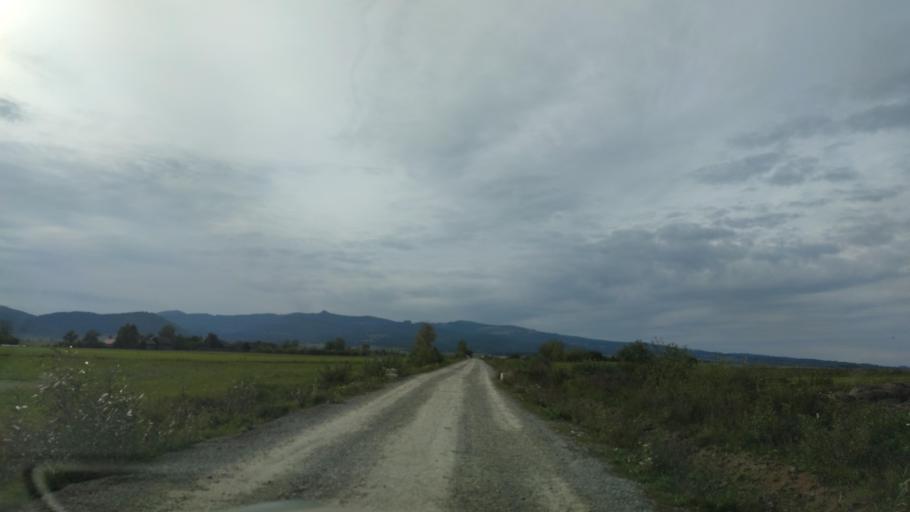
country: RO
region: Harghita
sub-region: Comuna Remetea
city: Remetea
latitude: 46.8163
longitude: 25.4201
